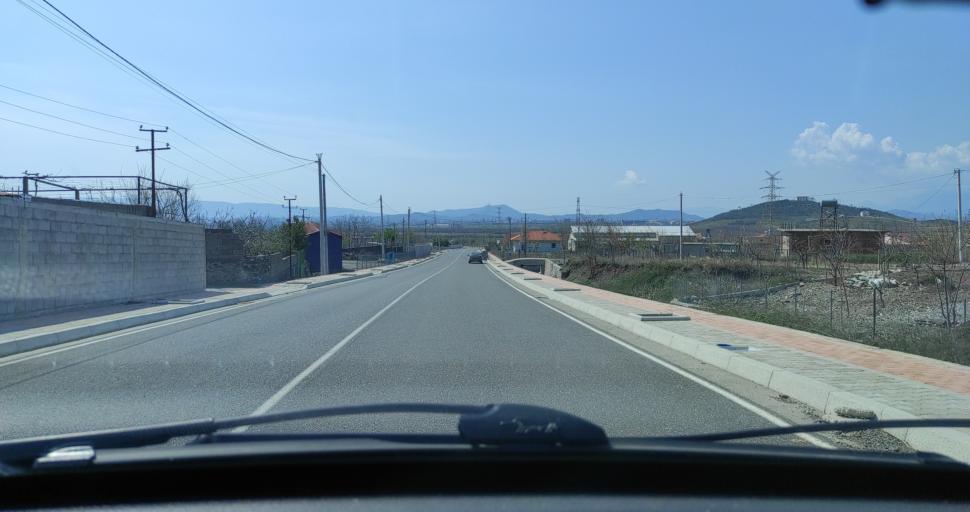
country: AL
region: Shkoder
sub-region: Rrethi i Shkodres
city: Vau i Dejes
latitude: 41.9988
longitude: 19.6476
